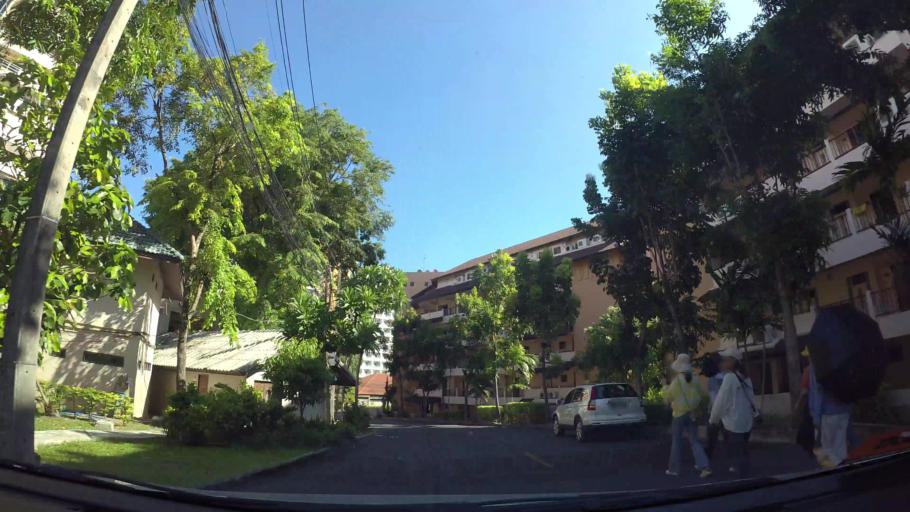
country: TH
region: Chon Buri
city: Phatthaya
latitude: 12.9066
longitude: 100.8708
